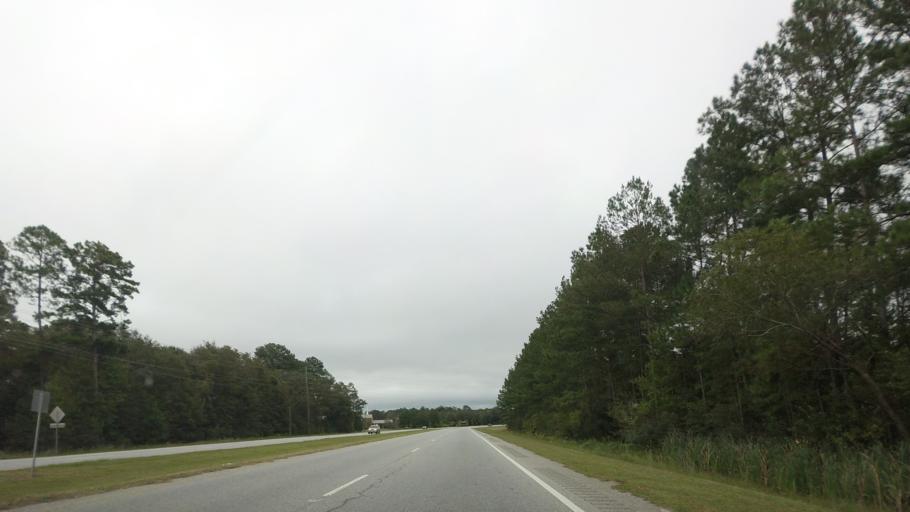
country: US
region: Georgia
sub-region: Lowndes County
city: Valdosta
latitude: 30.8812
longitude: -83.2476
